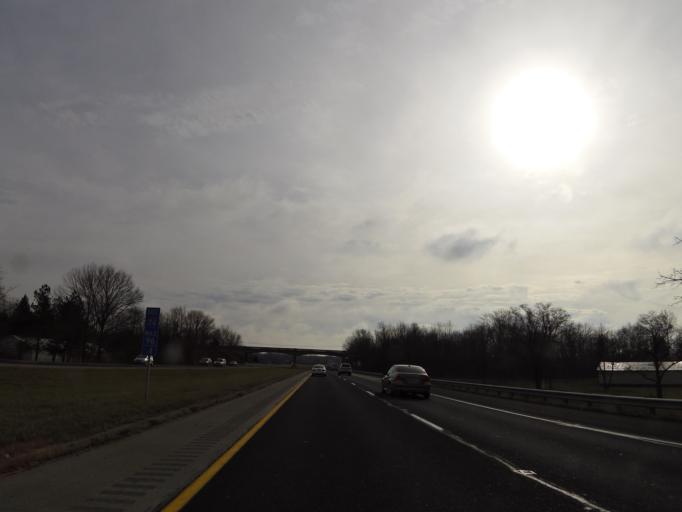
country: US
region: Indiana
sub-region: Marion County
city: Cumberland
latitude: 39.7111
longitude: -86.0036
